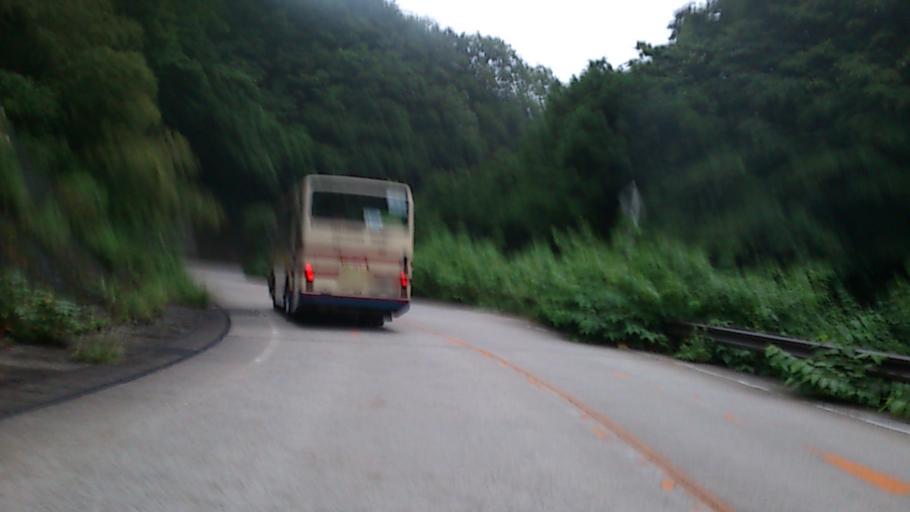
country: JP
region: Fukushima
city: Fukushima-shi
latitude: 37.7481
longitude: 140.3284
